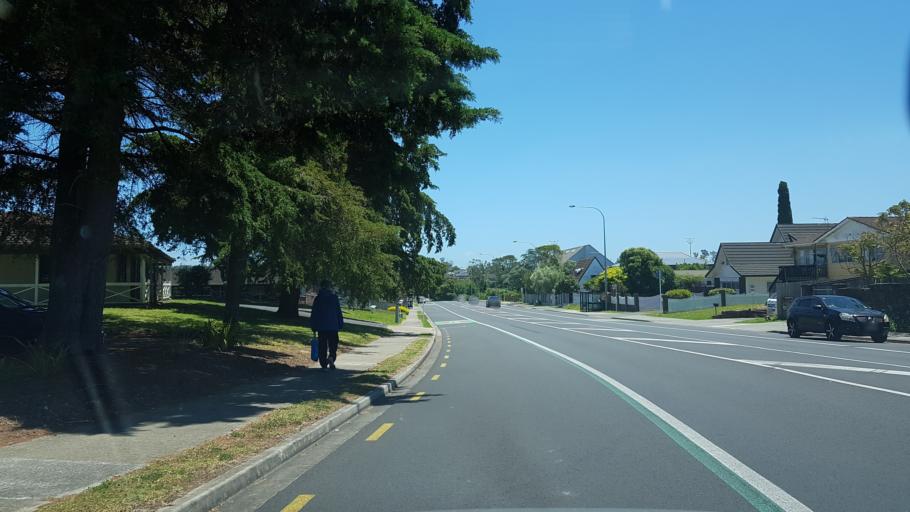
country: NZ
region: Auckland
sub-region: Auckland
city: North Shore
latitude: -36.7958
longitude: 174.7536
